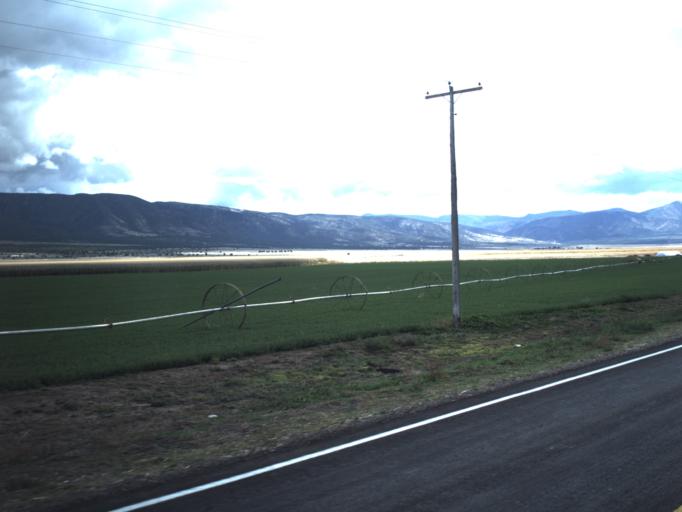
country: US
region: Utah
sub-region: Millard County
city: Fillmore
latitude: 38.8729
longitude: -112.4143
